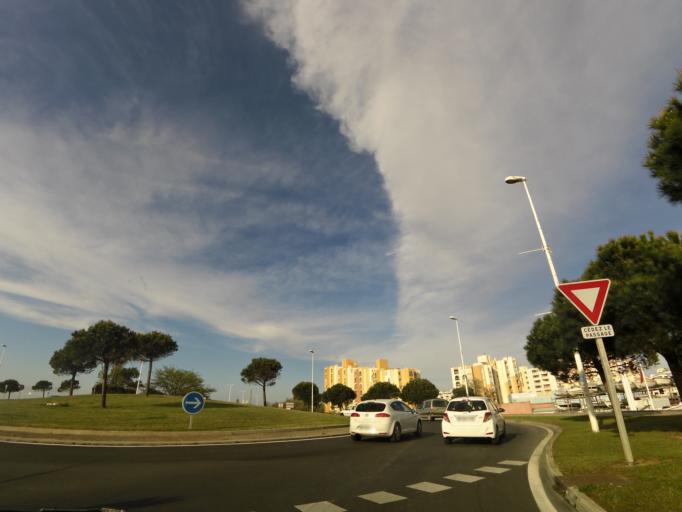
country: FR
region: Languedoc-Roussillon
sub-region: Departement de l'Herault
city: Perols
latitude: 43.5457
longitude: 3.9708
